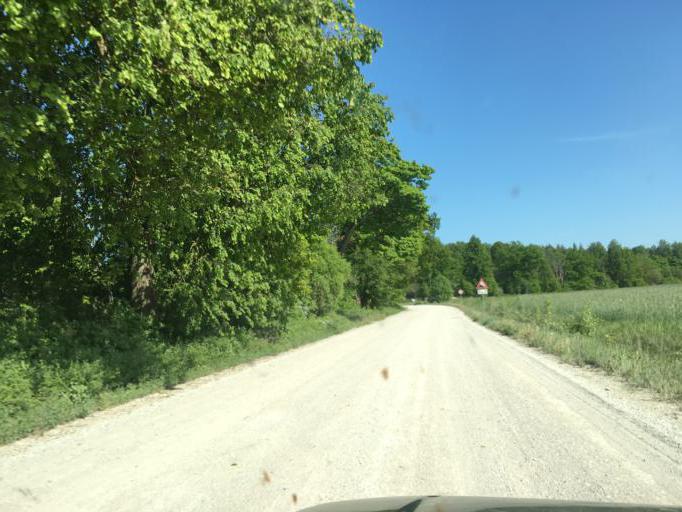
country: LV
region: Dundaga
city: Dundaga
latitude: 57.6075
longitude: 22.4621
